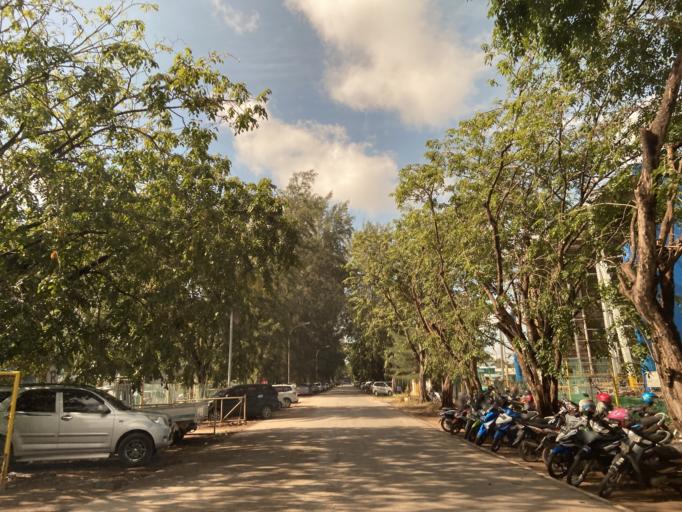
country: SG
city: Singapore
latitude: 1.1729
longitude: 104.0073
